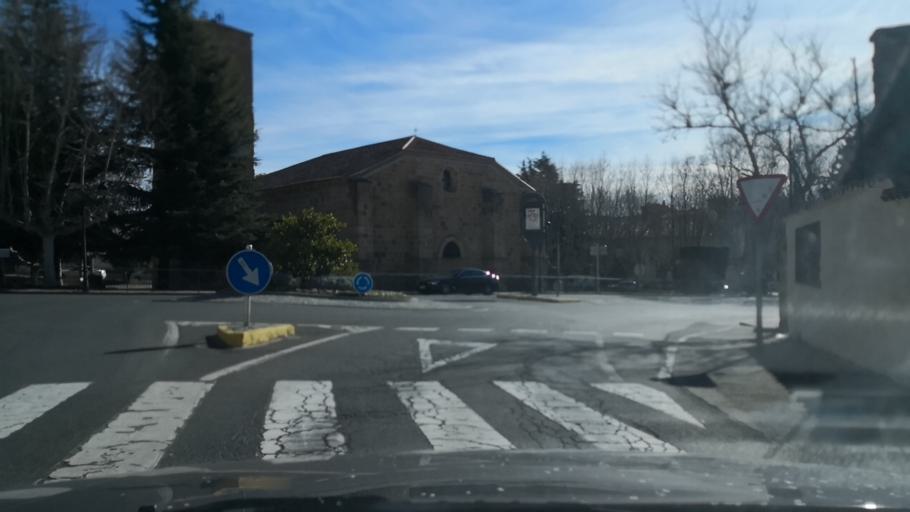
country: ES
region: Castille and Leon
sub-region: Provincia de Avila
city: Avila
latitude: 40.6522
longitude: -4.7029
